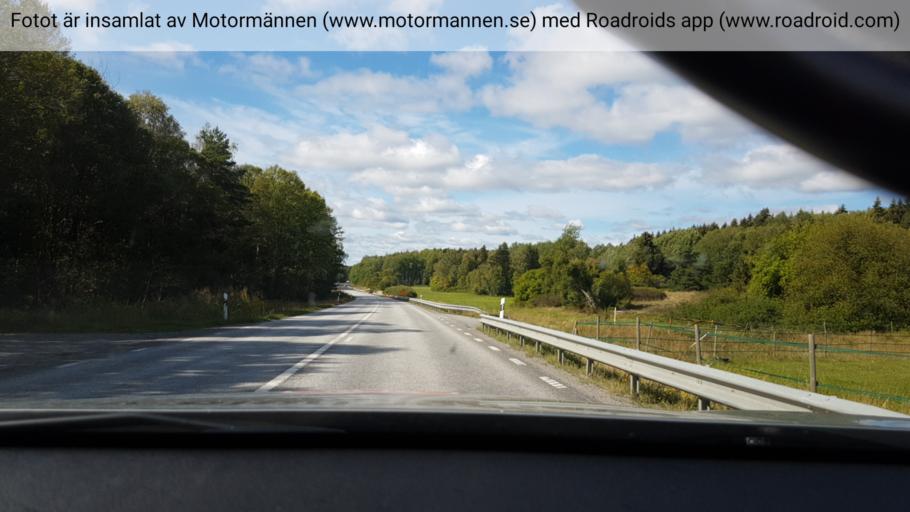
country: SE
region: Stockholm
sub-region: Vaxholms Kommun
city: Resaro
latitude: 59.4248
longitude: 18.2774
